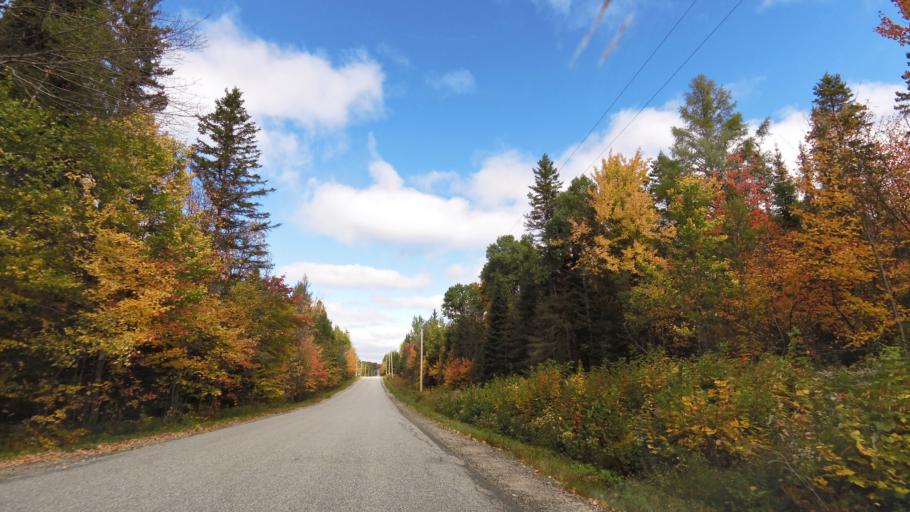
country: CA
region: Ontario
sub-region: Nipissing District
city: North Bay
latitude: 46.3594
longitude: -79.4871
